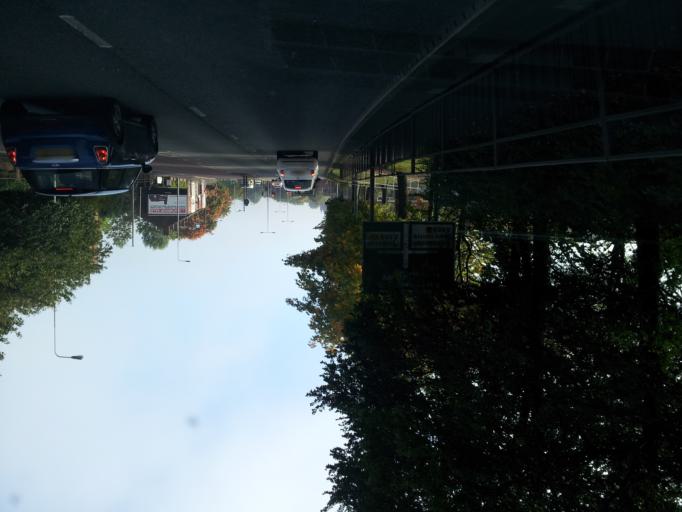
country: GB
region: England
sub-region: Borough of Oldham
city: Oldham
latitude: 53.5475
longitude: -2.1451
